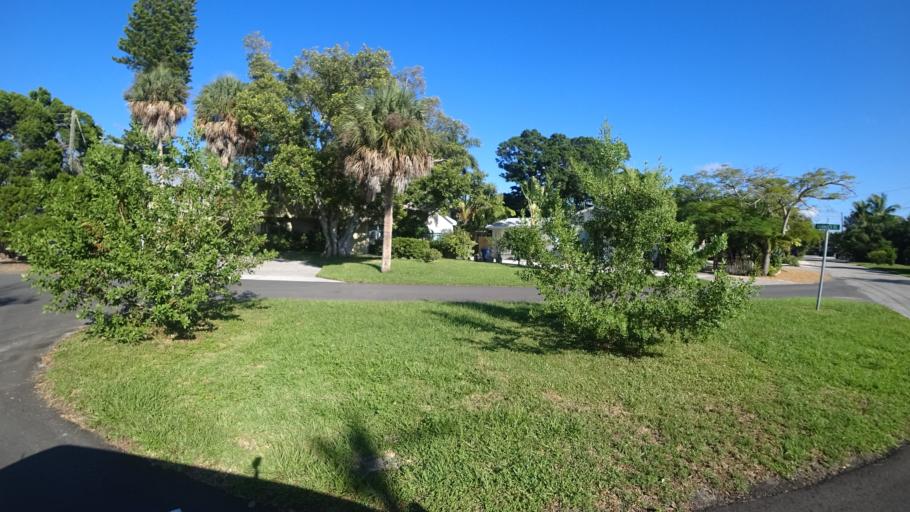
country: US
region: Florida
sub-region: Manatee County
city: Anna Maria
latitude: 27.5296
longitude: -82.7364
